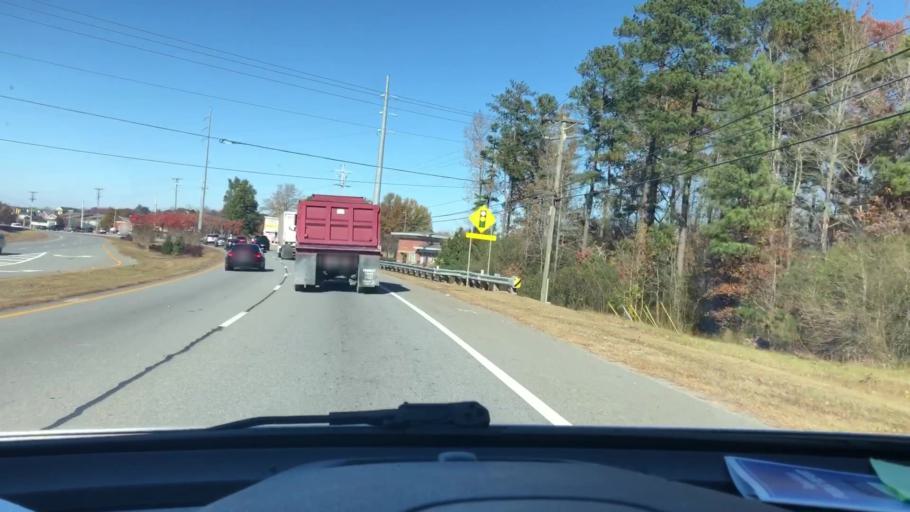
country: US
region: Georgia
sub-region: Fulton County
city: Johns Creek
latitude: 34.0819
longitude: -84.1611
